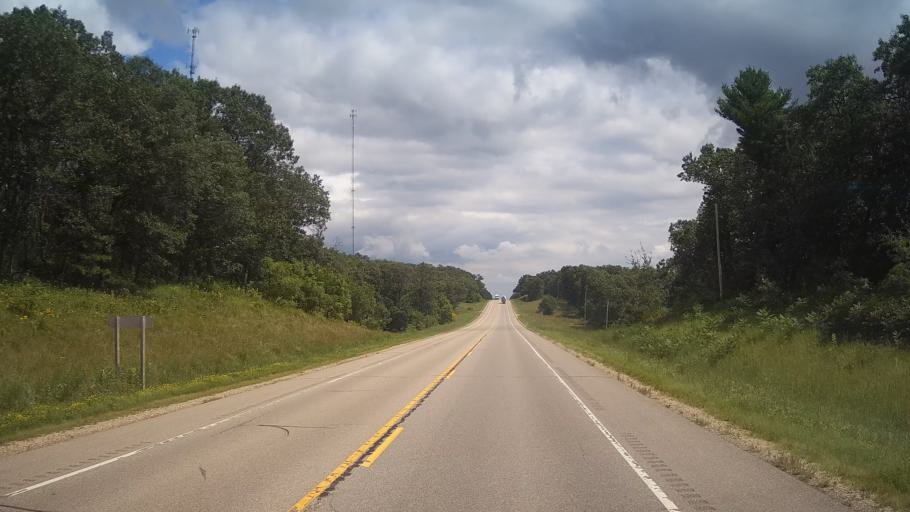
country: US
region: Wisconsin
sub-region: Marquette County
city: Westfield
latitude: 44.0218
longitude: -89.5648
